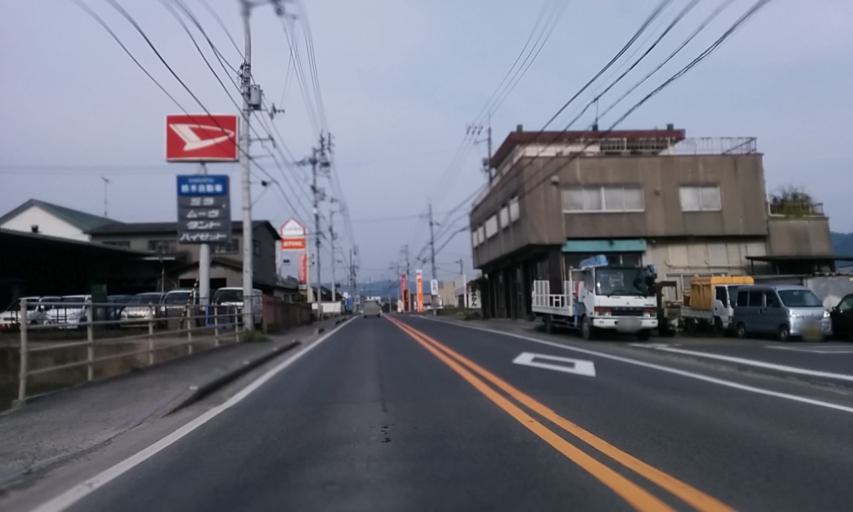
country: JP
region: Ehime
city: Niihama
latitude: 33.9562
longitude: 133.4272
